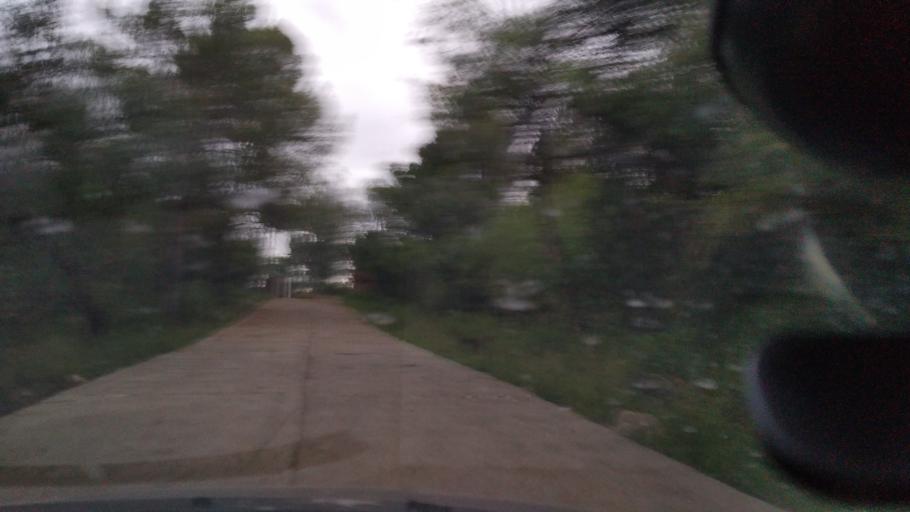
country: AR
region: Cordoba
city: Villa Las Rosas
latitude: -31.8791
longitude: -65.0247
